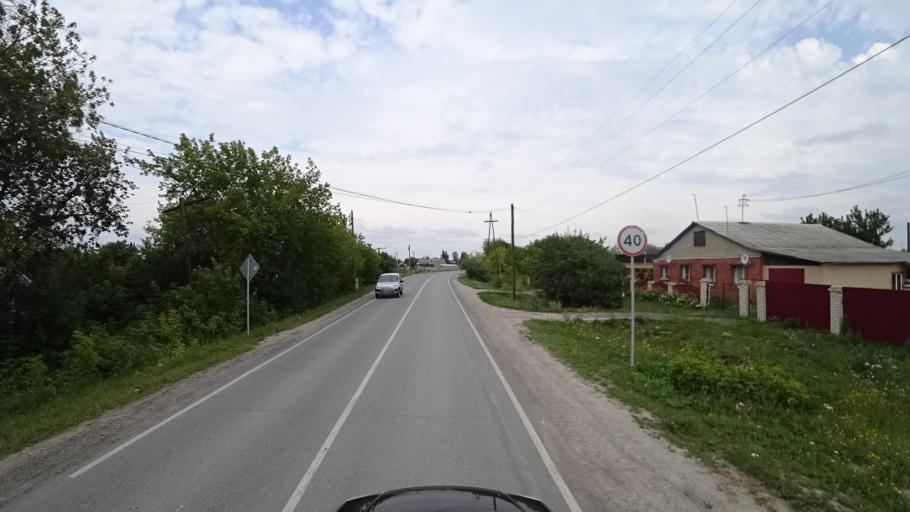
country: RU
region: Sverdlovsk
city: Kamyshlov
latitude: 56.8518
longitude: 62.7399
